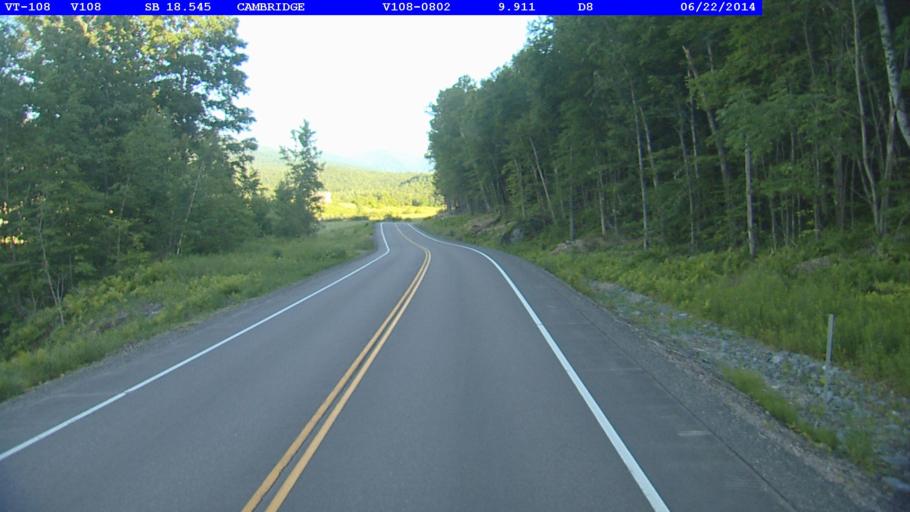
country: US
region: Vermont
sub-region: Lamoille County
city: Johnson
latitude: 44.6587
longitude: -72.8297
